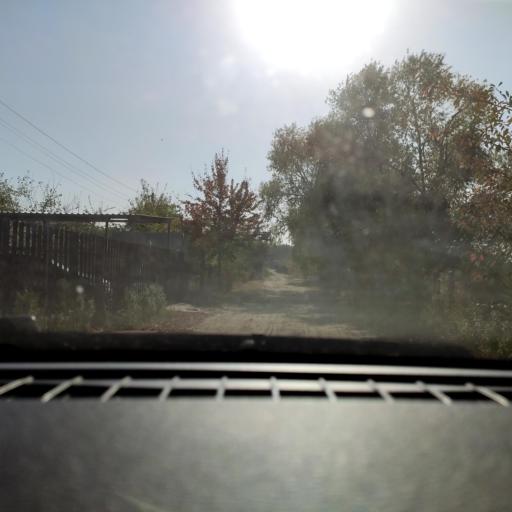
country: RU
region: Voronezj
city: Maslovka
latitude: 51.6080
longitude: 39.2164
